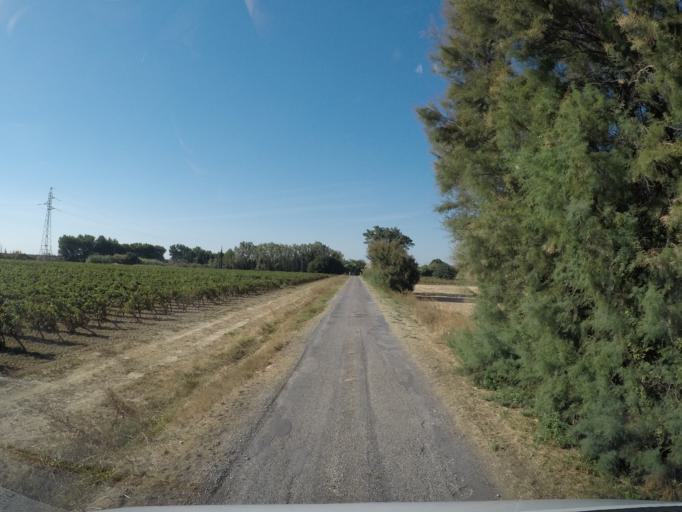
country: FR
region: Languedoc-Roussillon
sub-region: Departement de l'Aude
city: Narbonne
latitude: 43.1724
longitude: 3.0142
